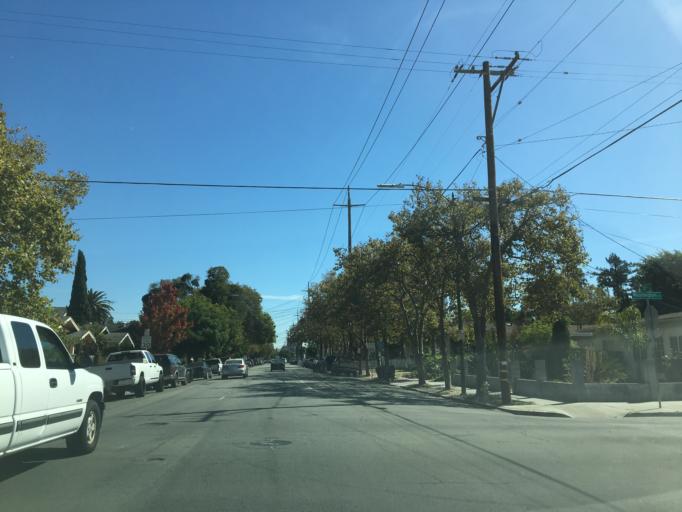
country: US
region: California
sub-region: Santa Clara County
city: San Jose
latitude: 37.3474
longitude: -121.8861
